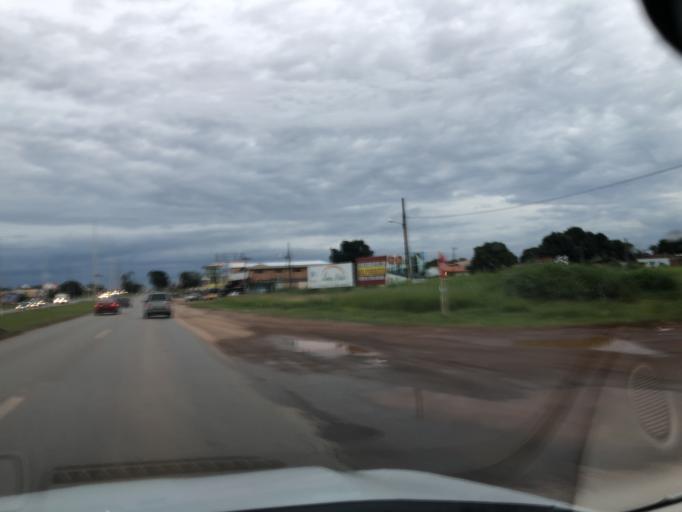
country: BR
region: Goias
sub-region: Luziania
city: Luziania
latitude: -16.1458
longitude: -47.9444
